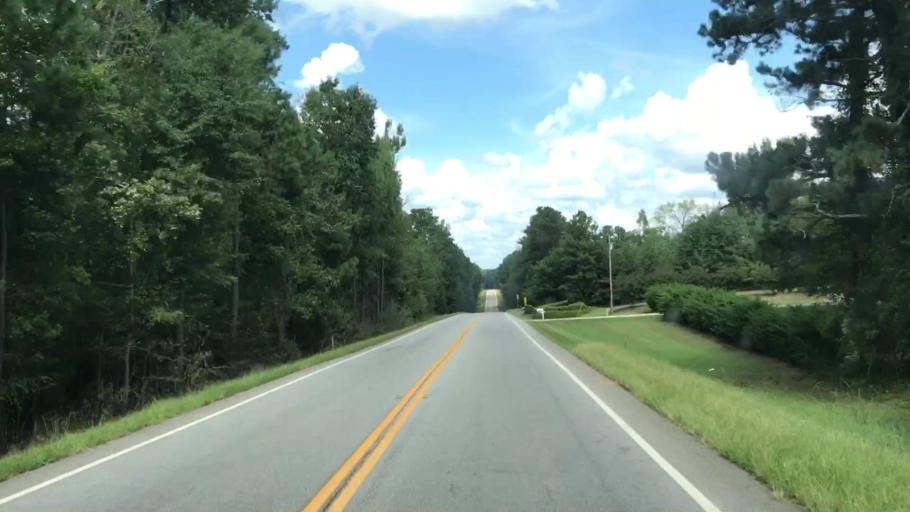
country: US
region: Georgia
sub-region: Greene County
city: Greensboro
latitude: 33.6205
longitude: -83.2119
